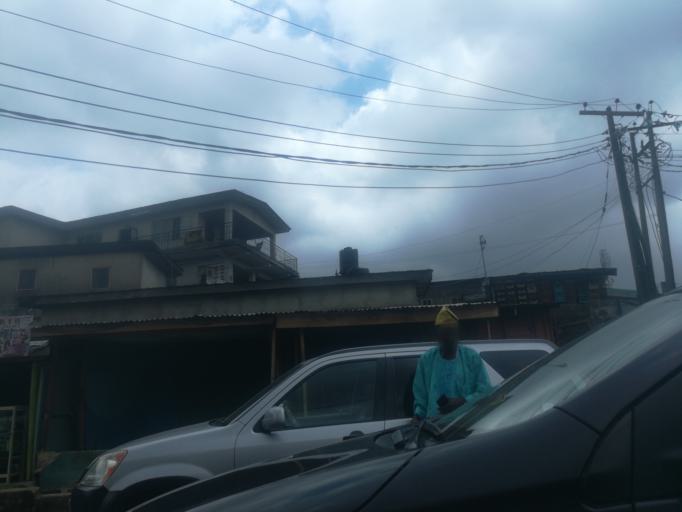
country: NG
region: Lagos
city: Somolu
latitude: 6.5567
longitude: 3.3933
